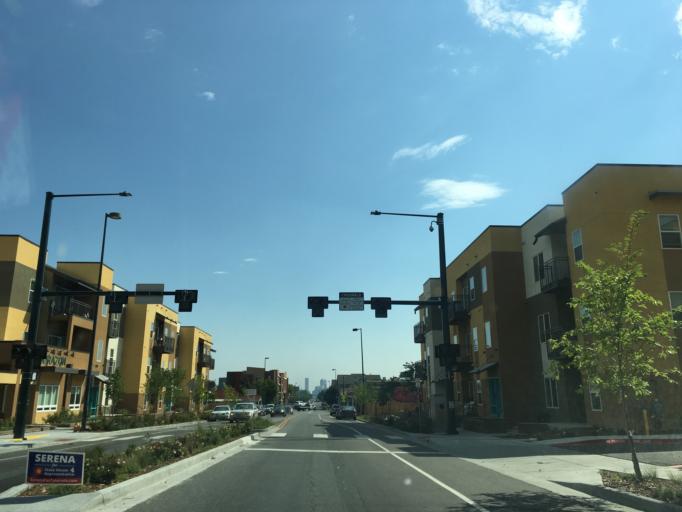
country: US
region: Colorado
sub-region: Jefferson County
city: Lakewood
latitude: 39.7029
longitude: -105.0446
